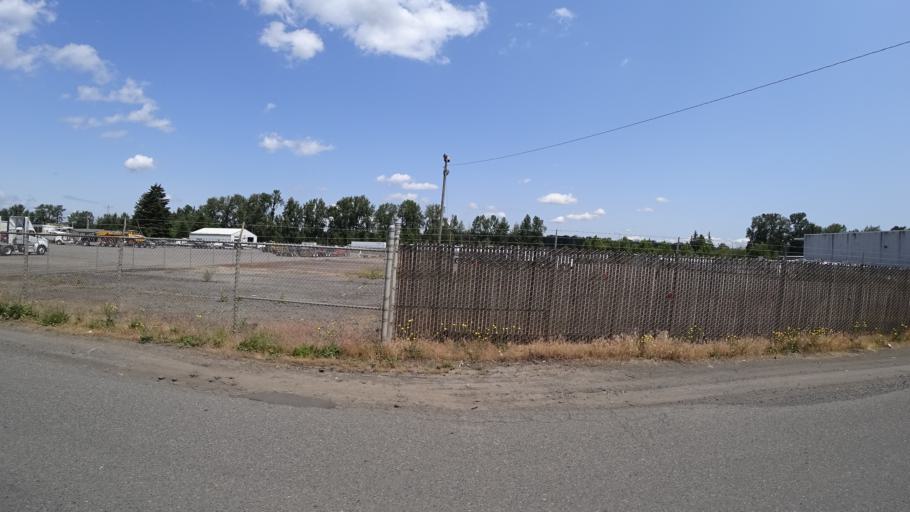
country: US
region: Washington
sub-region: Clark County
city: Vancouver
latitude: 45.6143
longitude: -122.7103
